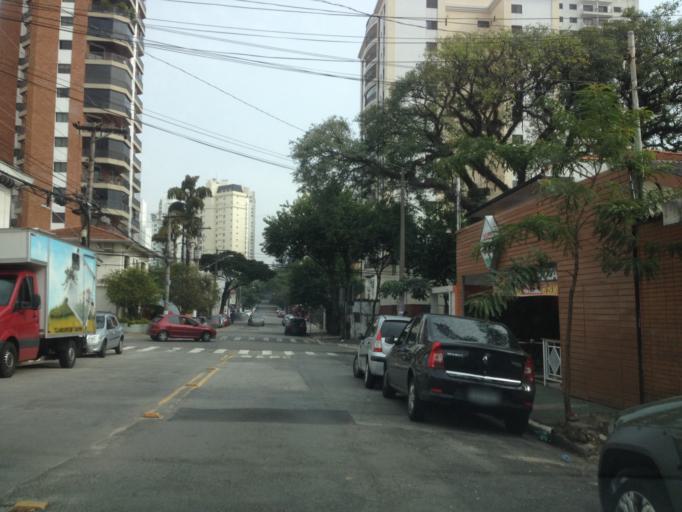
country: BR
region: Sao Paulo
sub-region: Diadema
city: Diadema
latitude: -23.6209
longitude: -46.6708
